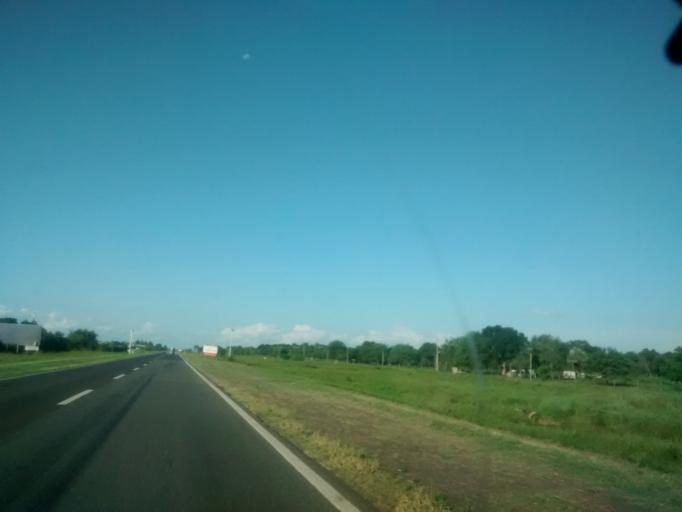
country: AR
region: Chaco
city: Fontana
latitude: -27.4807
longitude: -59.0621
